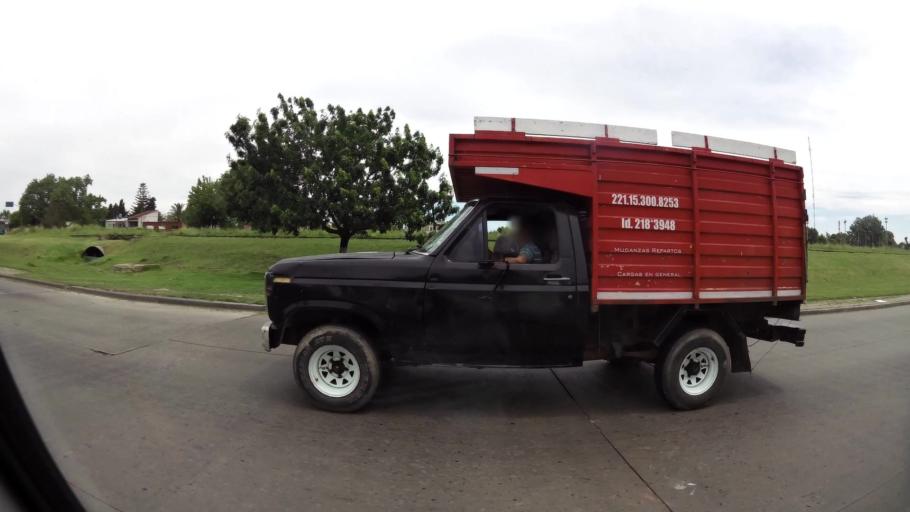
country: AR
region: Buenos Aires
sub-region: Partido de La Plata
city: La Plata
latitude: -34.9425
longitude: -57.9677
